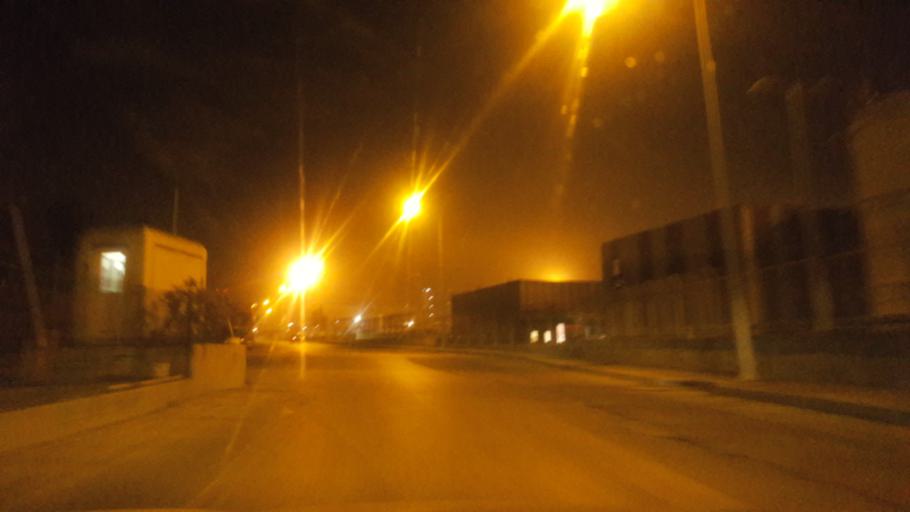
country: TR
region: Kocaeli
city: Tavsancil
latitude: 40.7736
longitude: 29.5271
